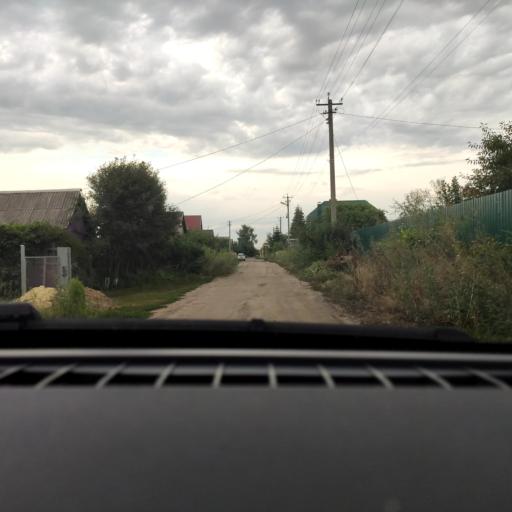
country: RU
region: Voronezj
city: Maslovka
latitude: 51.5212
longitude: 39.2329
